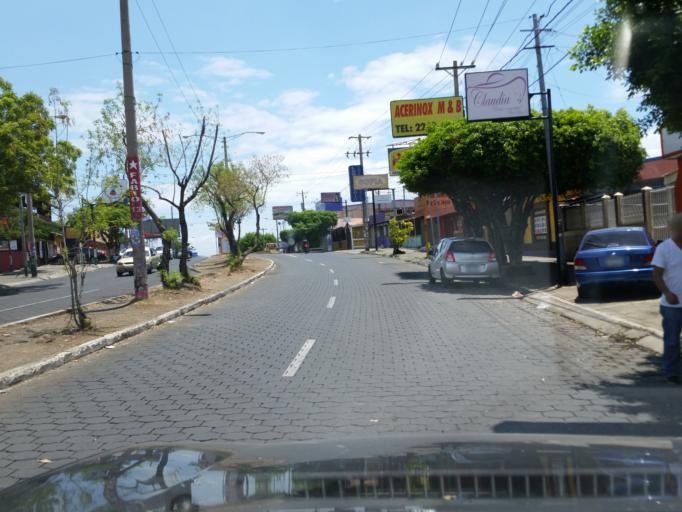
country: NI
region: Managua
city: Managua
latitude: 12.1451
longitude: -86.2279
